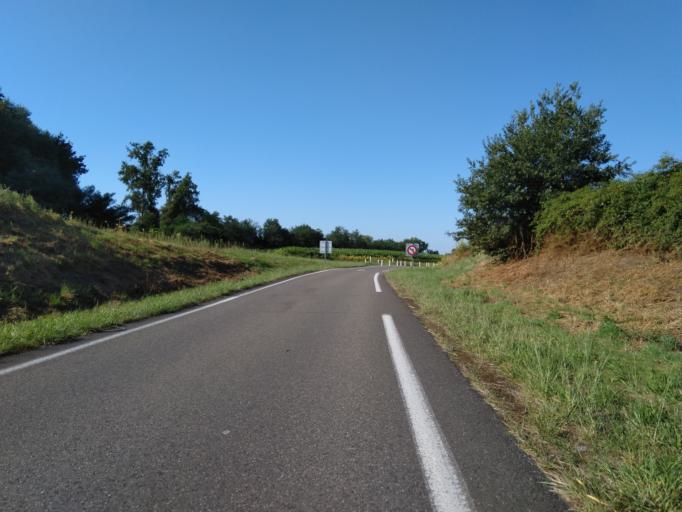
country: FR
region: Aquitaine
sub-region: Departement des Landes
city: Saint-Vincent-de-Paul
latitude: 43.7368
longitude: -1.0266
